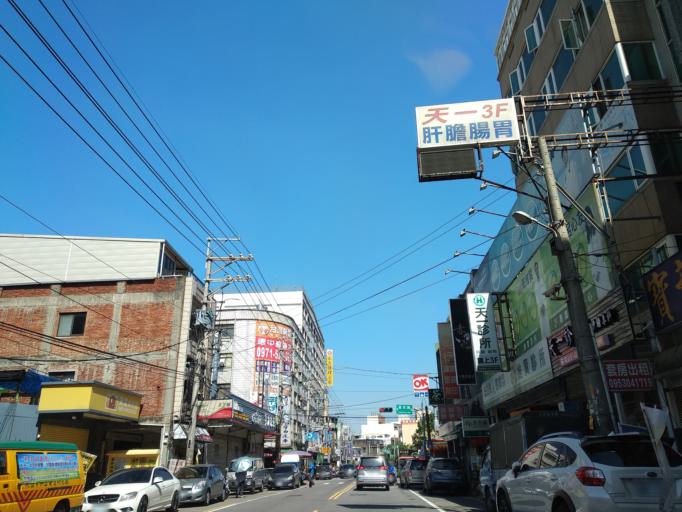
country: TW
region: Taiwan
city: Taoyuan City
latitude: 24.9472
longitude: 121.2205
